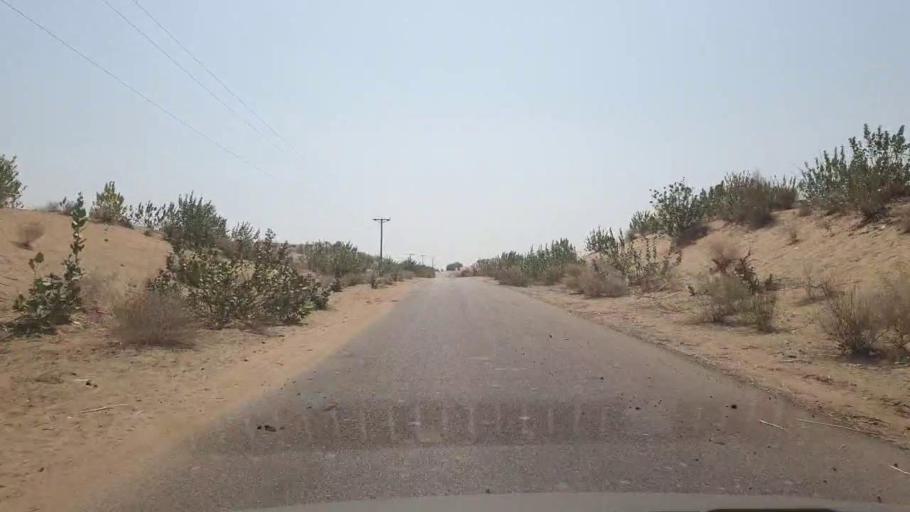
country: PK
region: Sindh
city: Chor
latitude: 25.6198
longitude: 70.1759
